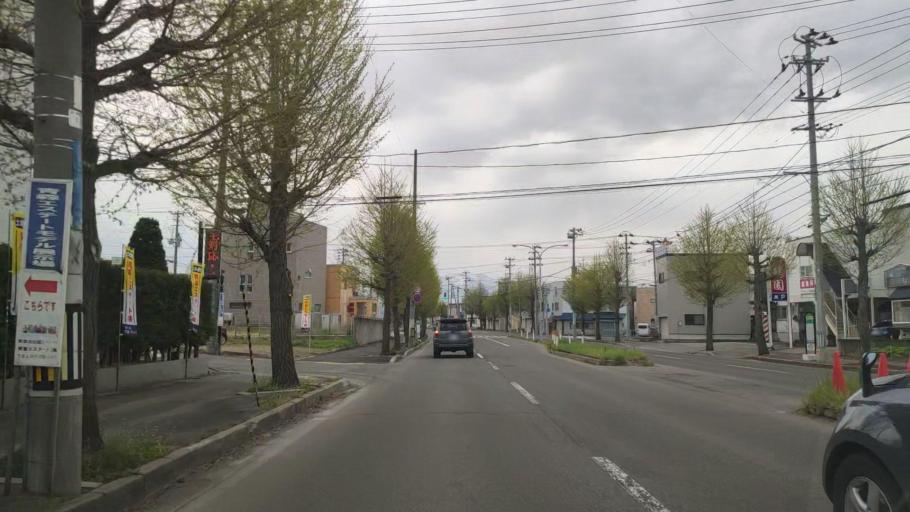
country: JP
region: Aomori
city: Aomori Shi
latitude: 40.8226
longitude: 140.7701
